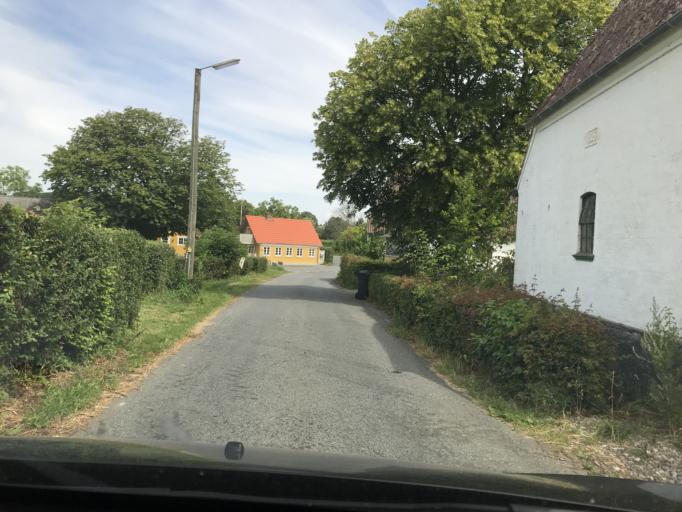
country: DK
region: South Denmark
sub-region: AEro Kommune
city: AEroskobing
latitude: 54.9126
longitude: 10.2813
